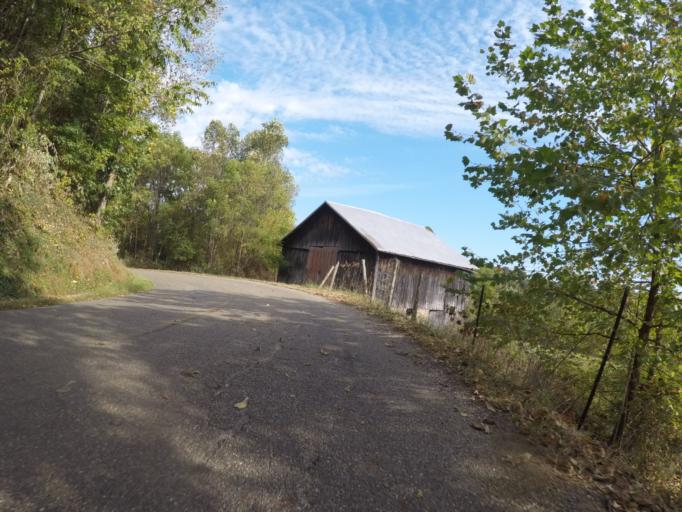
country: US
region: West Virginia
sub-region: Cabell County
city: Lesage
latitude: 38.5709
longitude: -82.4294
